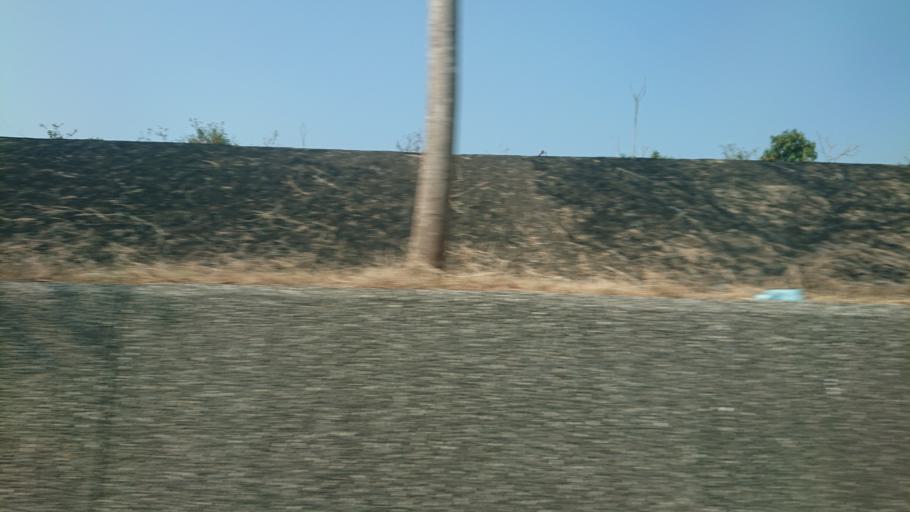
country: TW
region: Taiwan
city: Lugu
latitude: 23.7536
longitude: 120.6590
